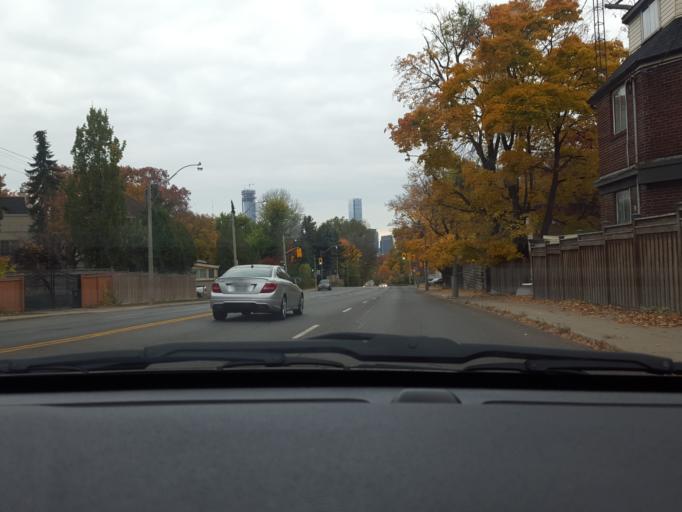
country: CA
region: Ontario
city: Toronto
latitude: 43.6893
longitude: -79.3832
